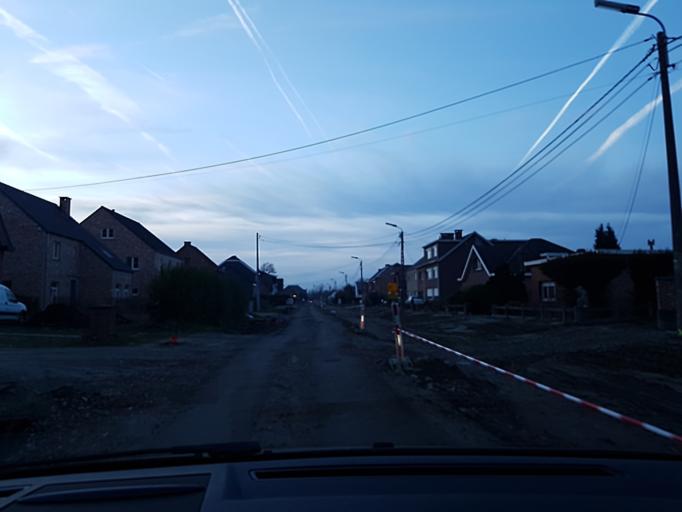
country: BE
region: Flanders
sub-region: Provincie Vlaams-Brabant
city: Haacht
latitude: 50.9735
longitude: 4.6503
